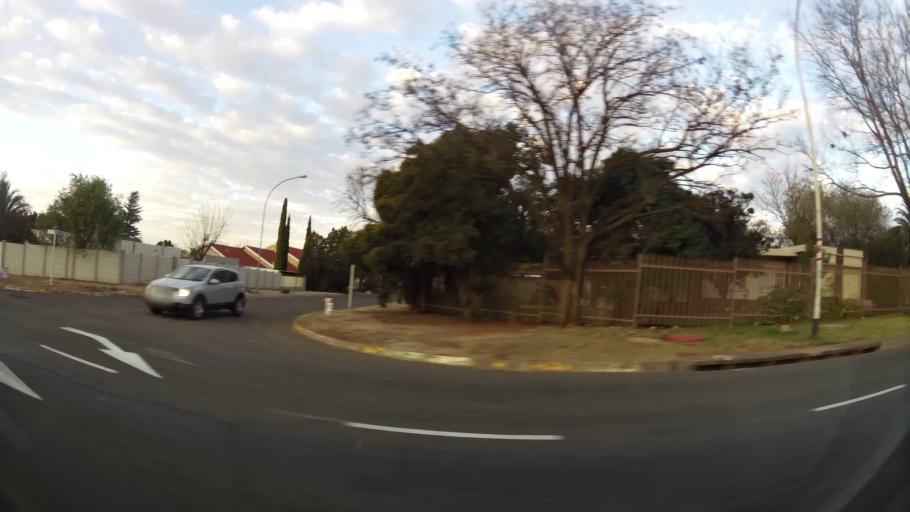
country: ZA
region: Orange Free State
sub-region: Mangaung Metropolitan Municipality
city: Bloemfontein
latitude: -29.1501
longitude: 26.1797
